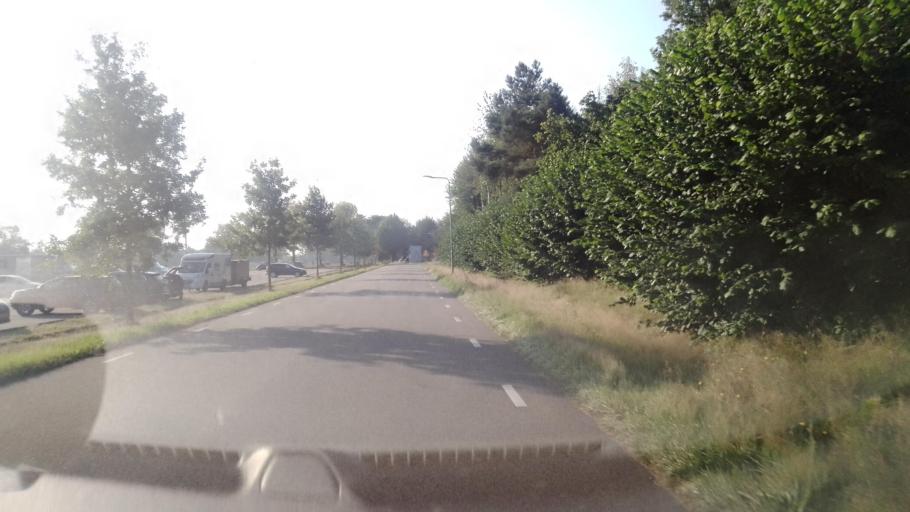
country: NL
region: Limburg
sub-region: Gemeente Peel en Maas
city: Maasbree
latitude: 51.4115
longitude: 5.9674
